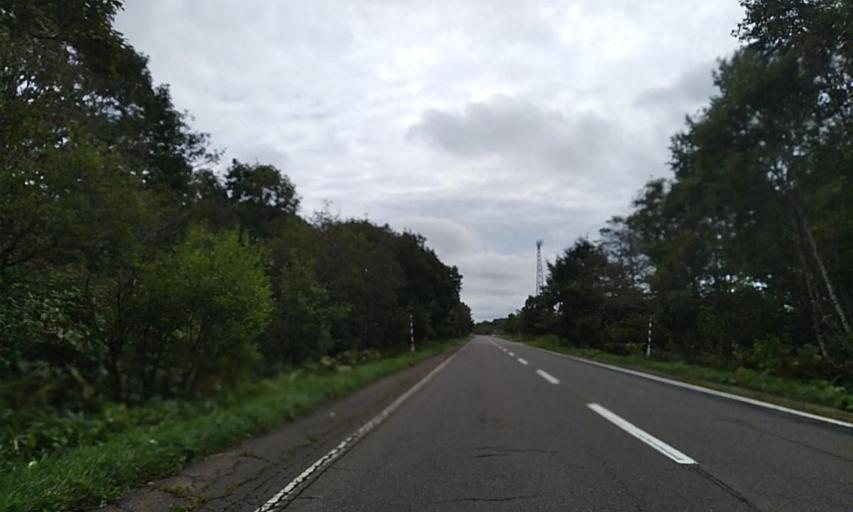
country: JP
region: Hokkaido
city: Shibetsu
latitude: 43.5462
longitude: 145.2288
